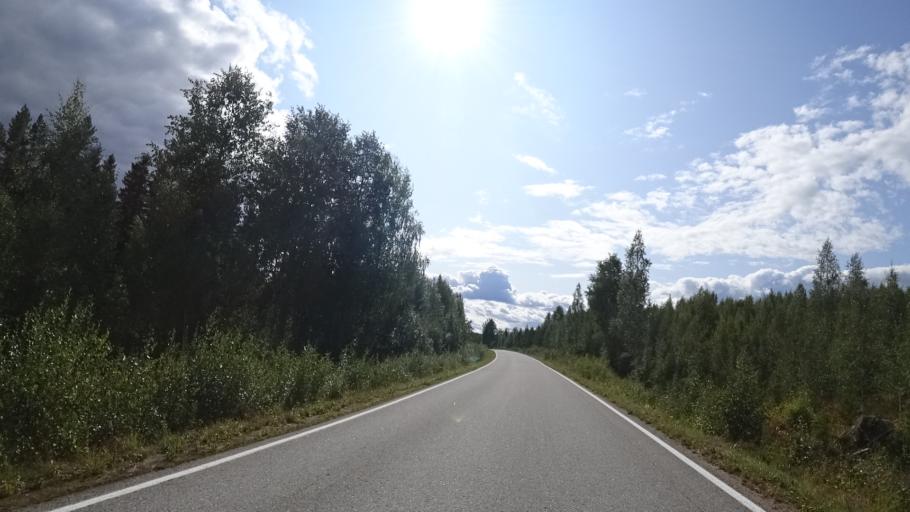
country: FI
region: North Karelia
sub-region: Joensuu
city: Ilomantsi
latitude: 62.4109
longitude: 30.9729
